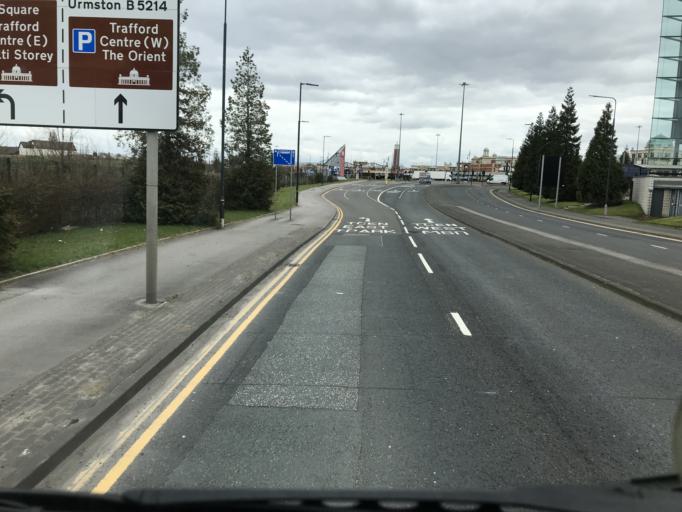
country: GB
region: England
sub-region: Trafford
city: Urmston
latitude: 53.4694
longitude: -2.3560
